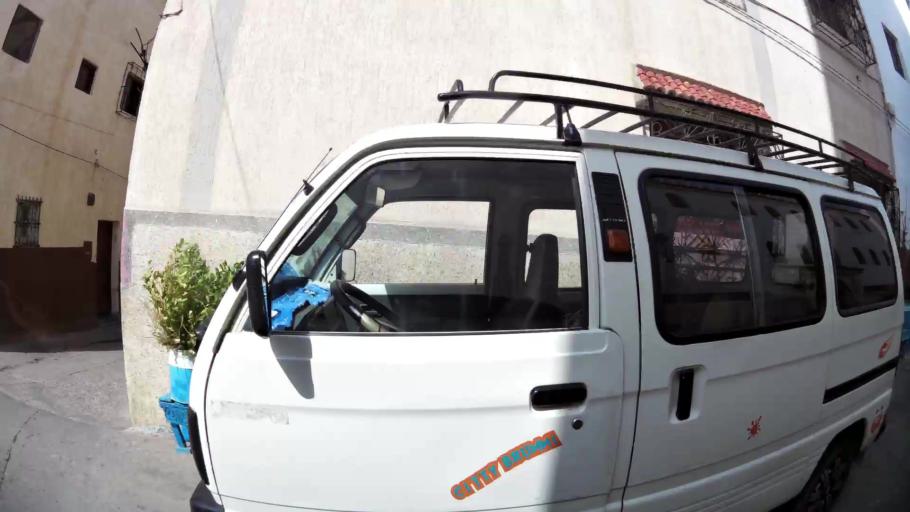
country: MA
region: Tanger-Tetouan
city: Tetouan
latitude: 35.5774
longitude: -5.3846
